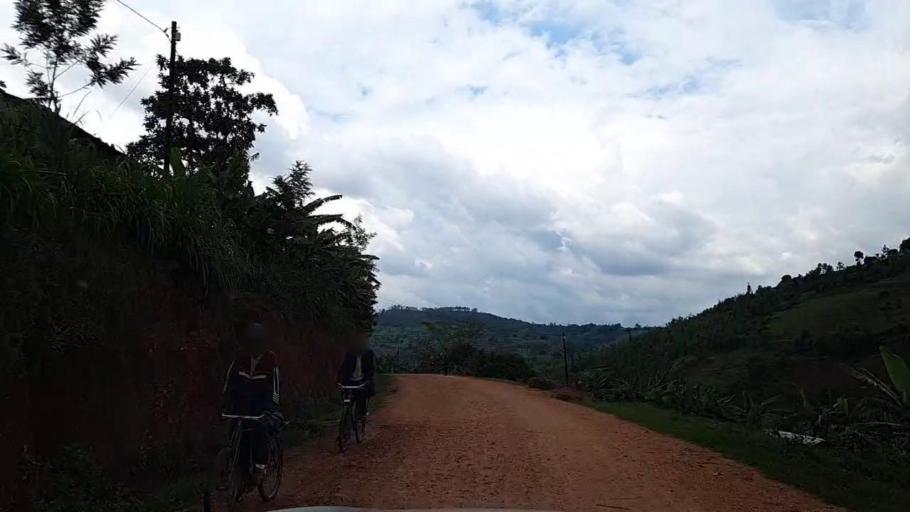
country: RW
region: Southern Province
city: Gikongoro
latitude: -2.4168
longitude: 29.6673
